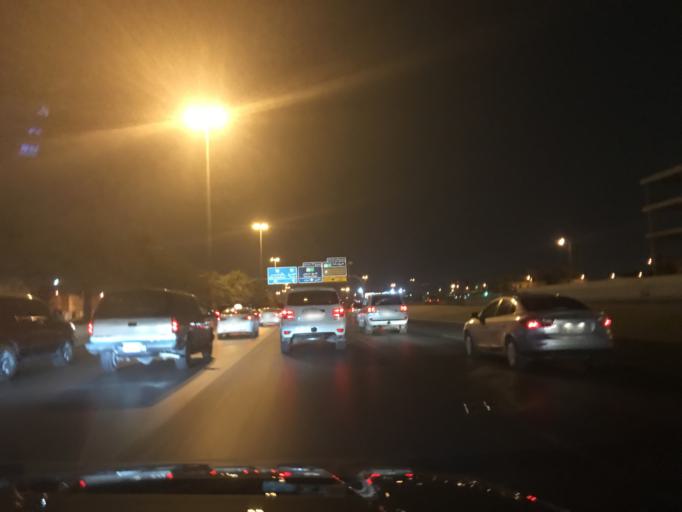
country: SA
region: Ar Riyad
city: Riyadh
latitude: 24.7212
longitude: 46.7582
